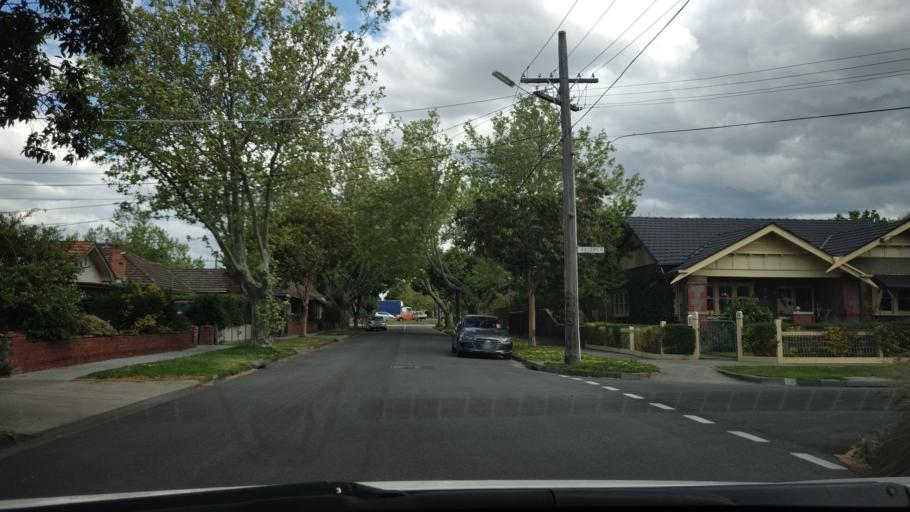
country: AU
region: Victoria
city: Carnegie
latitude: -37.8835
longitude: 145.0637
